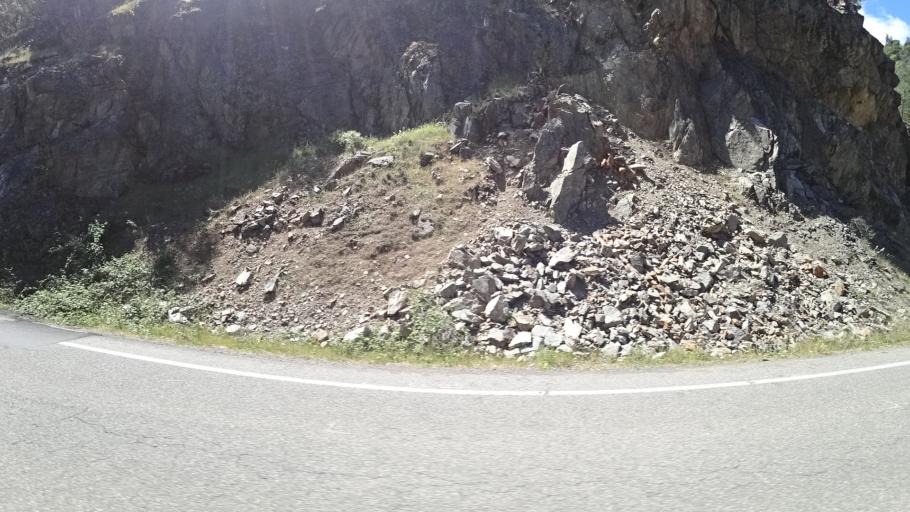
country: US
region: California
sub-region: Trinity County
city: Weaverville
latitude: 40.7670
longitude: -123.1368
